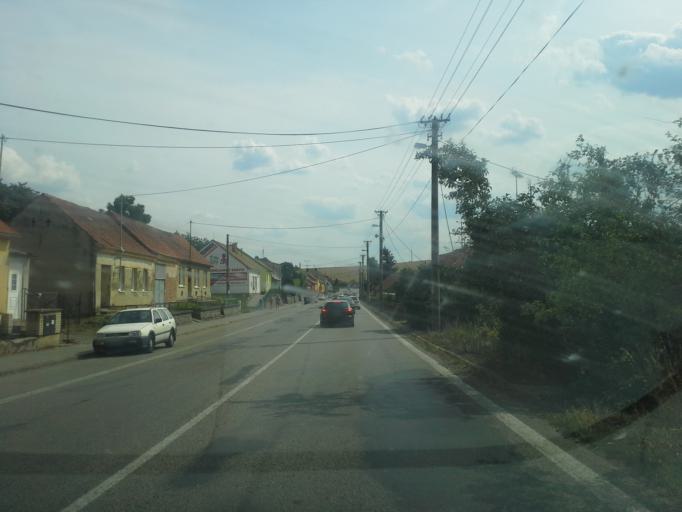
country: CZ
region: South Moravian
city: Lipuvka
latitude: 49.3564
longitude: 16.5518
